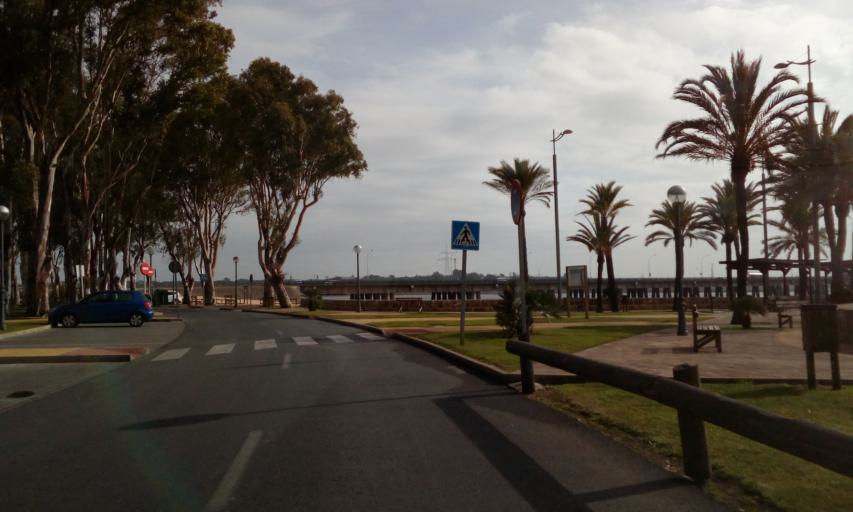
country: ES
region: Andalusia
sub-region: Provincia de Huelva
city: Punta Umbria
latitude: 37.2132
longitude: -6.9408
